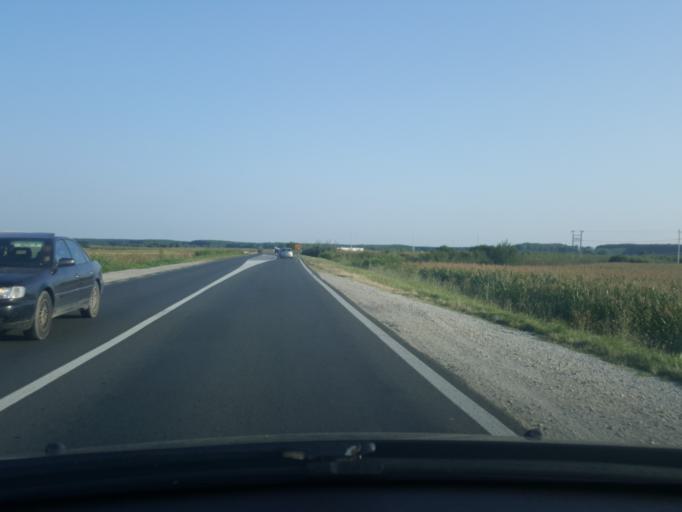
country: RS
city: Klenak
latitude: 44.7767
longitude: 19.7248
